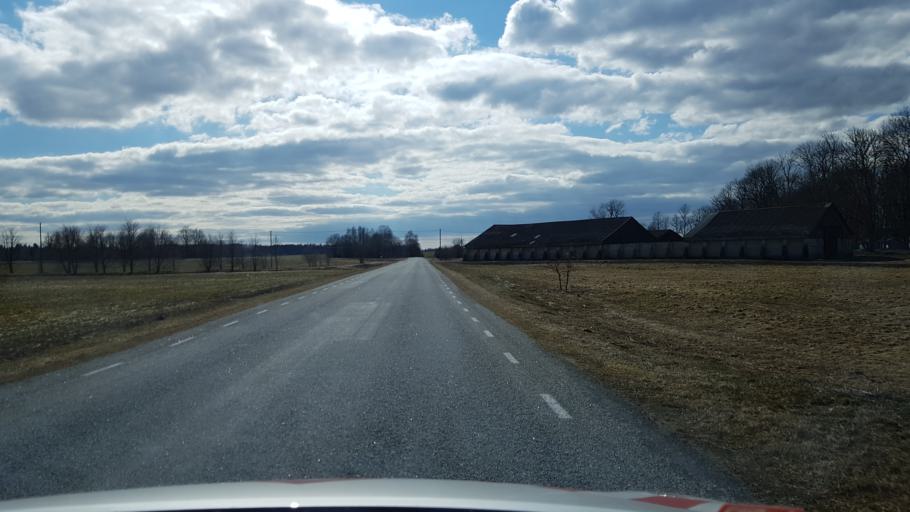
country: EE
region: Laeaene-Virumaa
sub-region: Rakvere linn
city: Rakvere
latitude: 59.3182
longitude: 26.2576
